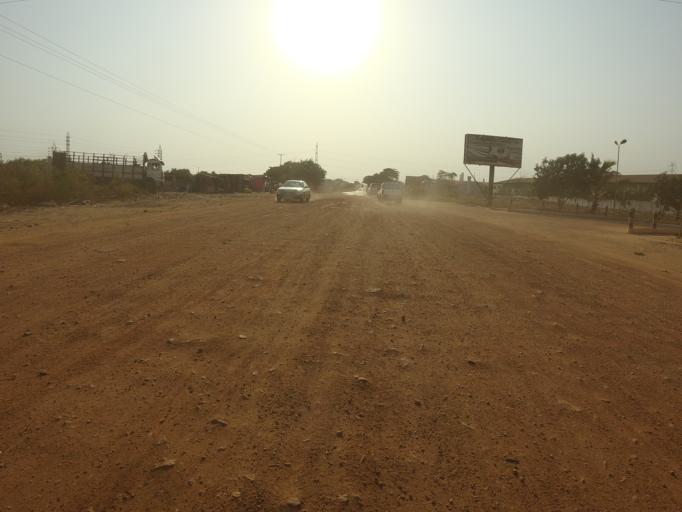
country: GH
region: Greater Accra
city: Tema
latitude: 5.6695
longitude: 0.0161
